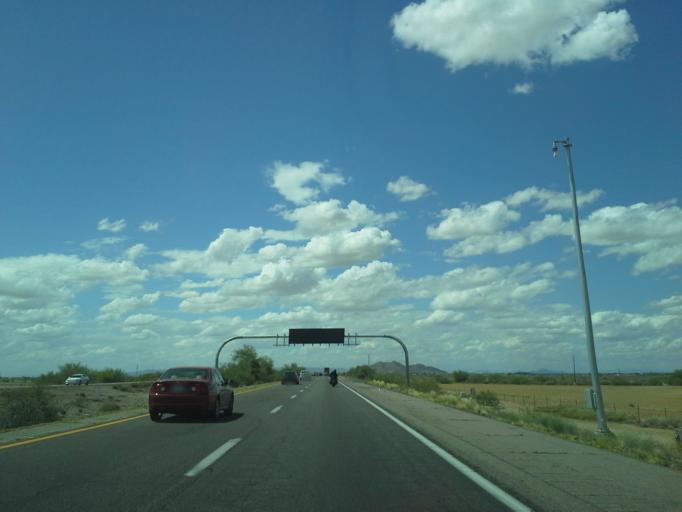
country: US
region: Arizona
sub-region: Pinal County
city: Casa Blanca
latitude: 33.0995
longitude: -111.8276
